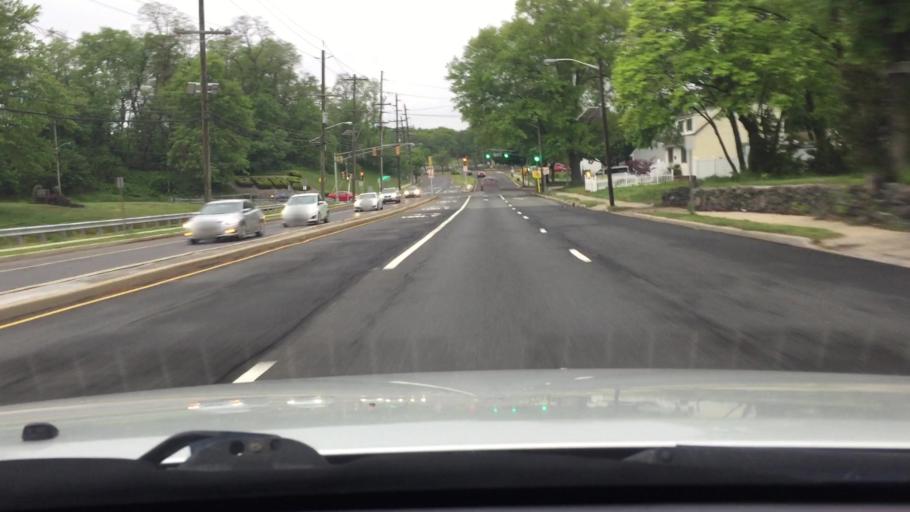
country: US
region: New Jersey
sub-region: Middlesex County
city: East Brunswick
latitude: 40.4343
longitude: -74.4004
